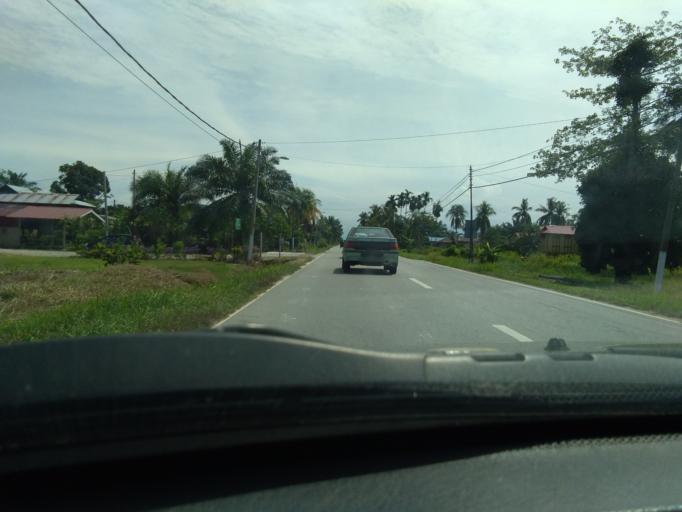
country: MY
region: Perak
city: Bagan Serai
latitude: 5.0260
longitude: 100.5544
